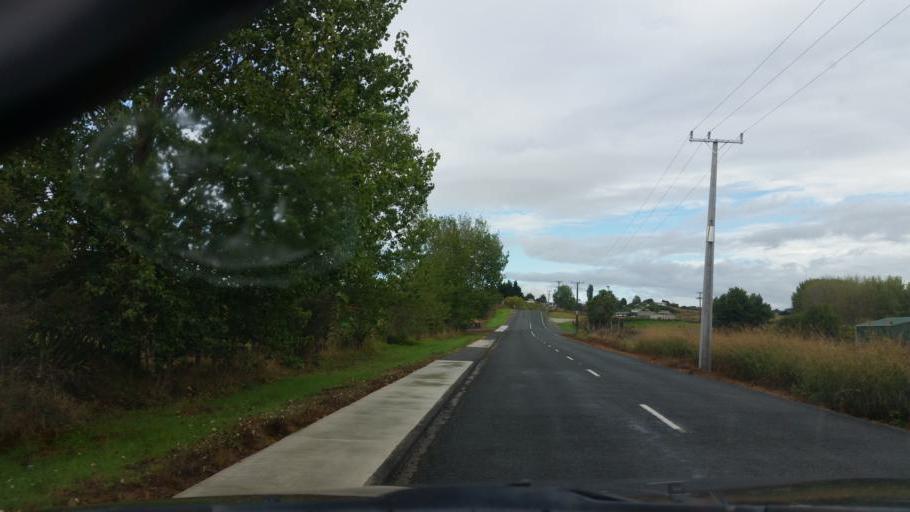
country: NZ
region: Northland
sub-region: Whangarei
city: Ruakaka
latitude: -36.1140
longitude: 174.3653
